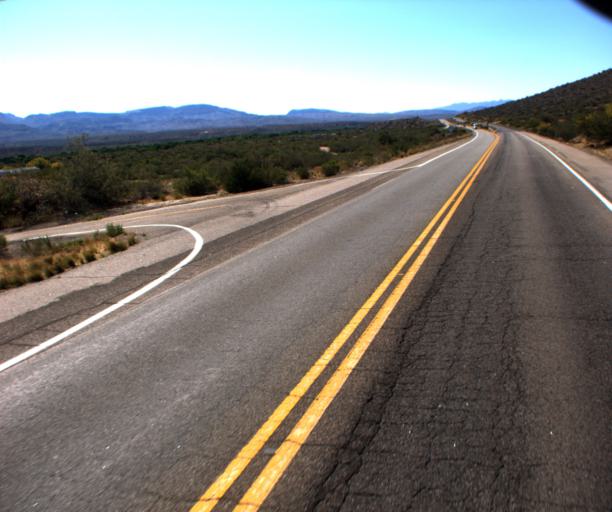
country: US
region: Arizona
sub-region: Yavapai County
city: Bagdad
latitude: 34.6918
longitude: -113.6050
